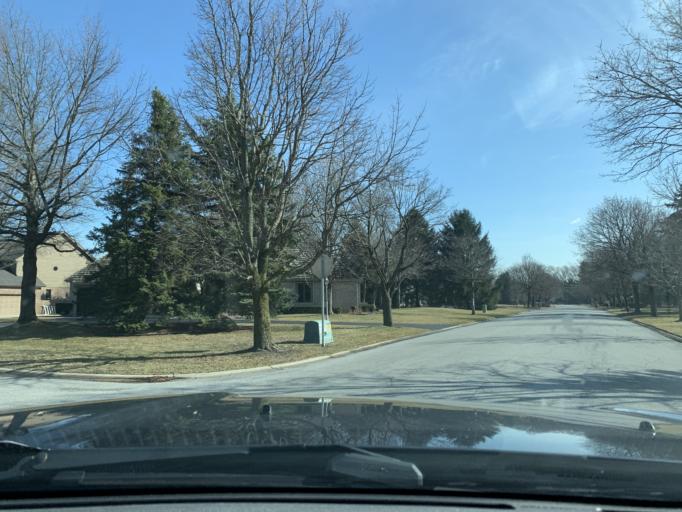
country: US
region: Indiana
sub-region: Lake County
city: Dyer
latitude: 41.5179
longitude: -87.4896
